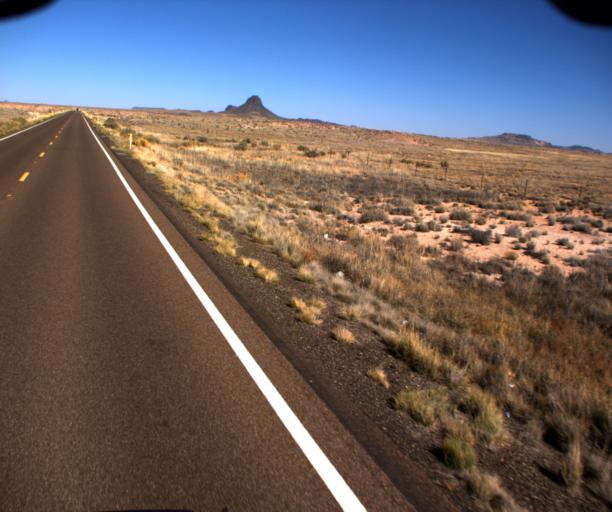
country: US
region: Arizona
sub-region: Navajo County
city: Dilkon
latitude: 35.2468
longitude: -110.4301
